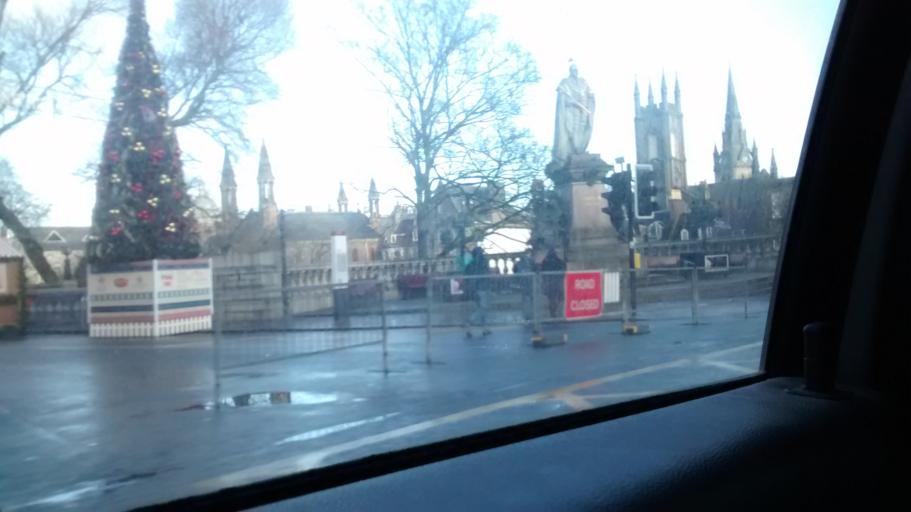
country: GB
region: Scotland
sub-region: Aberdeen City
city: Aberdeen
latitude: 57.1456
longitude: -2.1025
